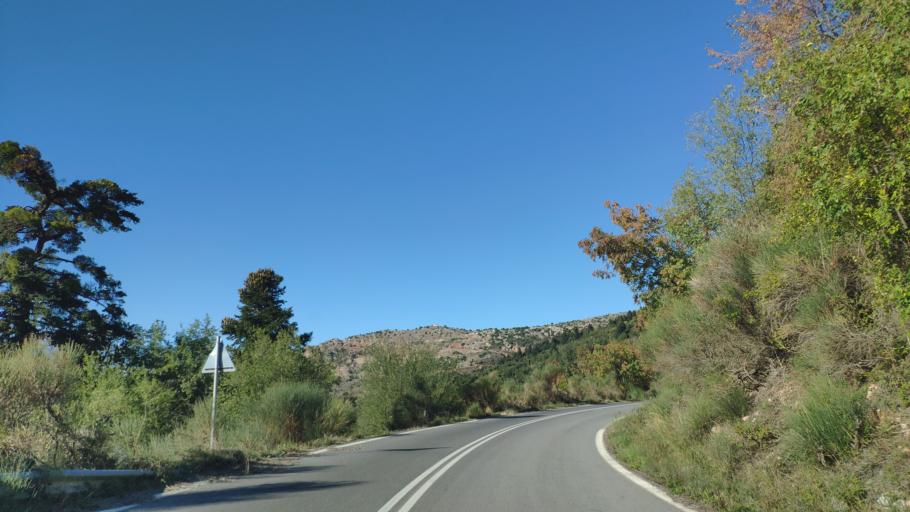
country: GR
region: Peloponnese
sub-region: Nomos Arkadias
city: Dimitsana
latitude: 37.5712
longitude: 22.0613
